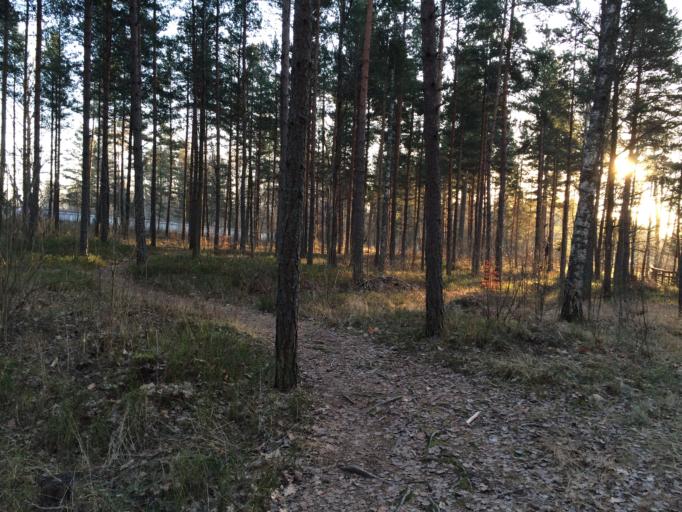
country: SE
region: Vaestmanland
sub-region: Hallstahammars Kommun
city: Hallstahammar
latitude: 59.6144
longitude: 16.2024
